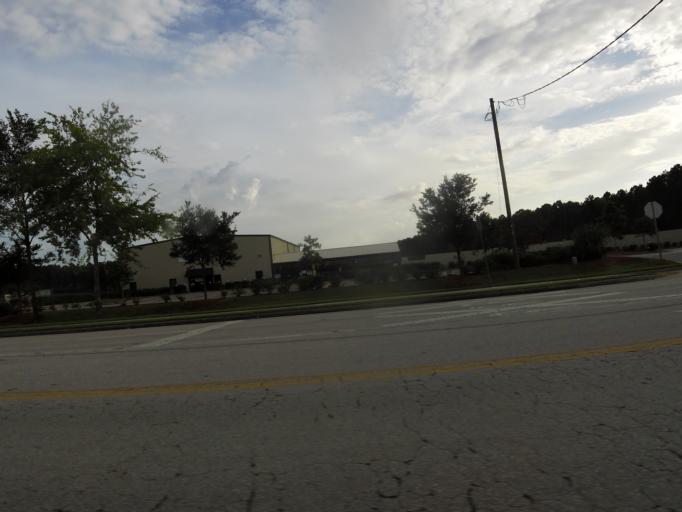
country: US
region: Florida
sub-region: Duval County
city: Jacksonville
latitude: 30.3380
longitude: -81.7694
